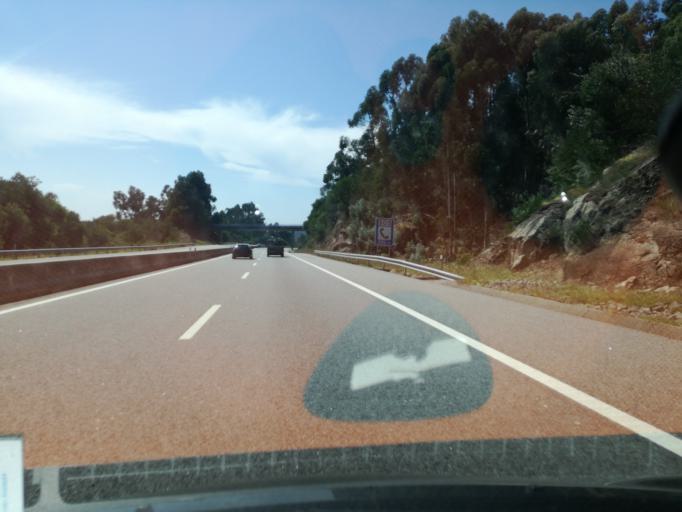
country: PT
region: Viana do Castelo
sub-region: Viana do Castelo
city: Meadela
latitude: 41.7596
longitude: -8.7951
